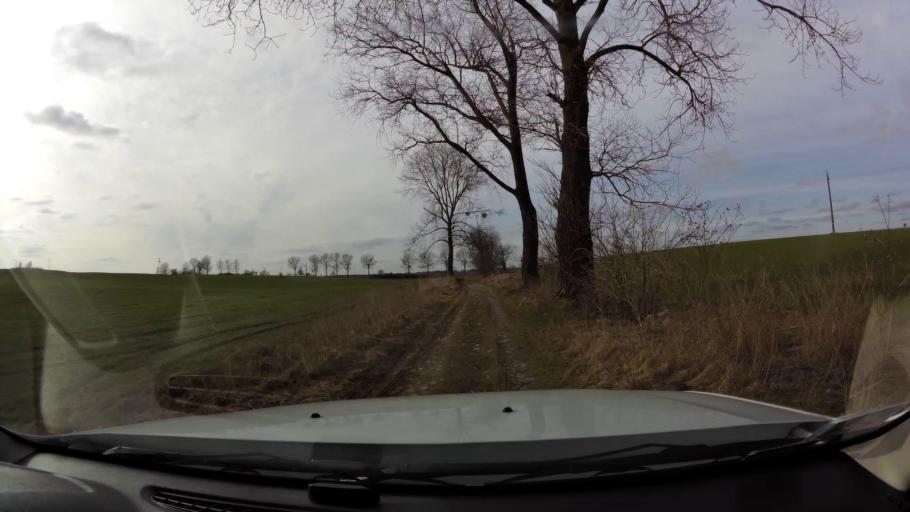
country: PL
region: West Pomeranian Voivodeship
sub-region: Powiat drawski
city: Drawsko Pomorskie
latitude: 53.5238
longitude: 15.7652
